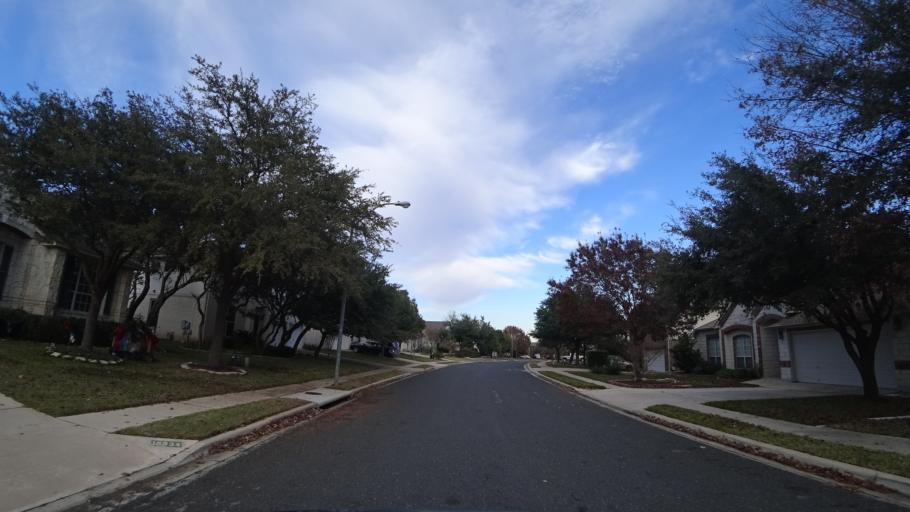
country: US
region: Texas
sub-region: Williamson County
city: Brushy Creek
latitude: 30.4989
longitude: -97.7375
